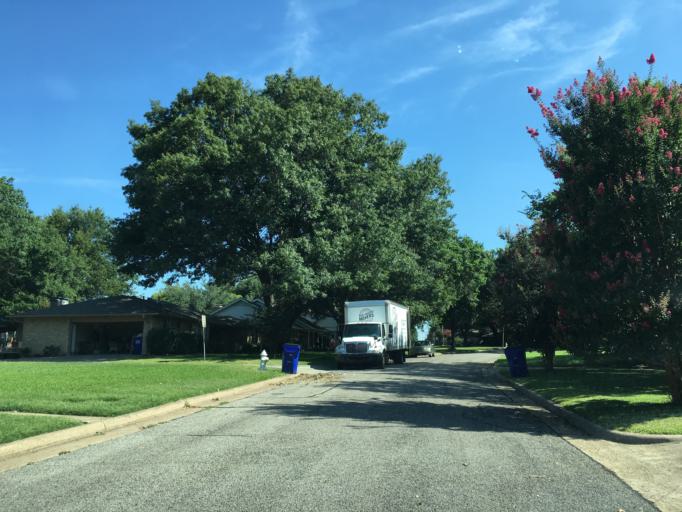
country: US
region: Texas
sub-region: Dallas County
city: Farmers Branch
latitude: 32.9166
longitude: -96.8792
